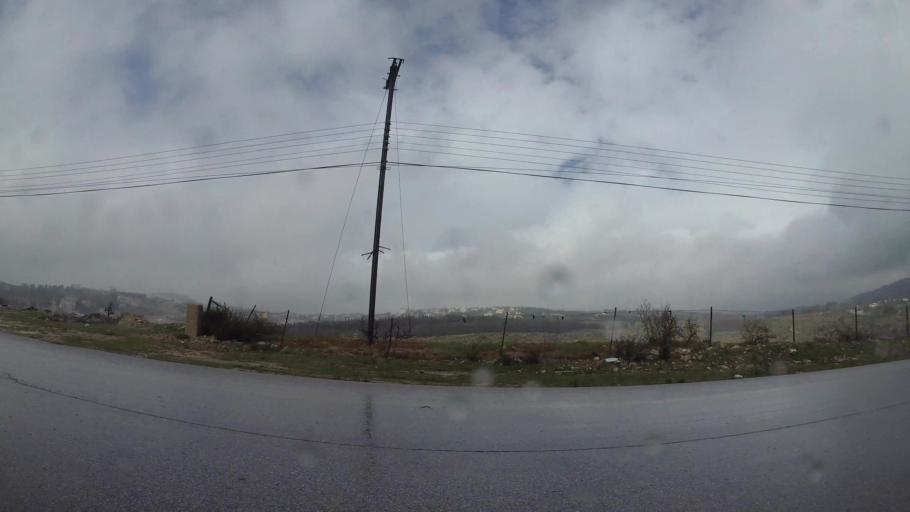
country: JO
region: Amman
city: Al Jubayhah
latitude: 32.0145
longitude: 35.8039
